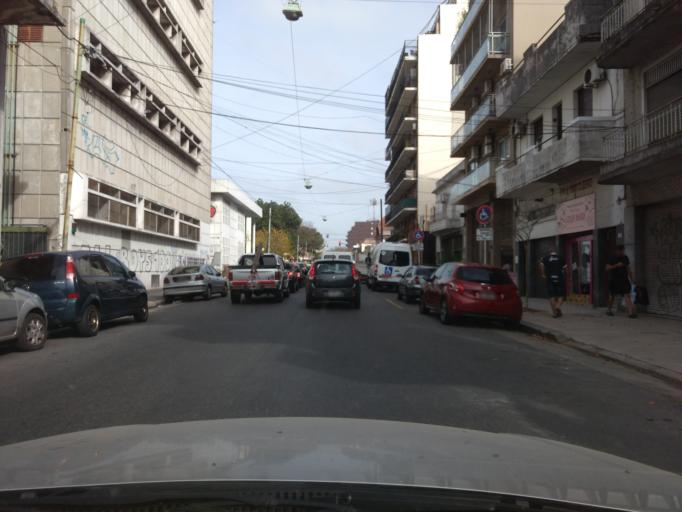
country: AR
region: Buenos Aires F.D.
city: Villa Santa Rita
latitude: -34.6169
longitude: -58.5004
